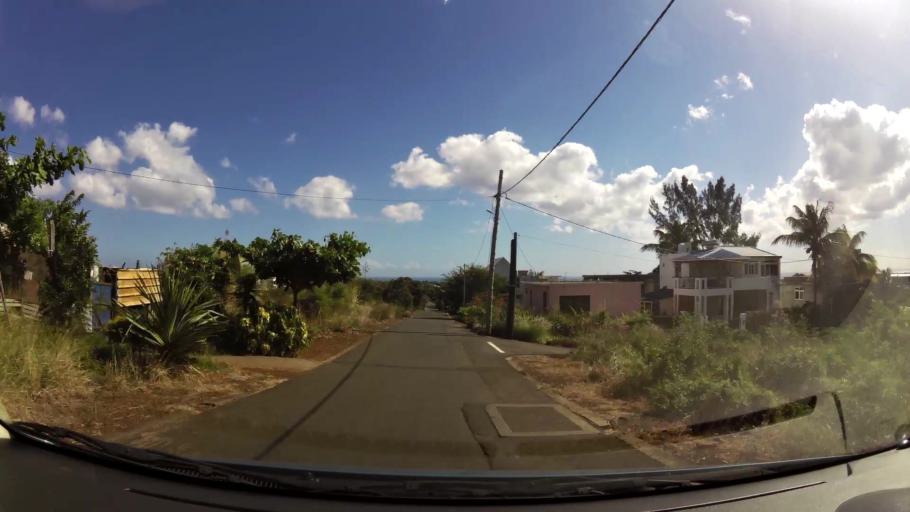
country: MU
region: Black River
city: Cascavelle
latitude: -20.2645
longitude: 57.4200
